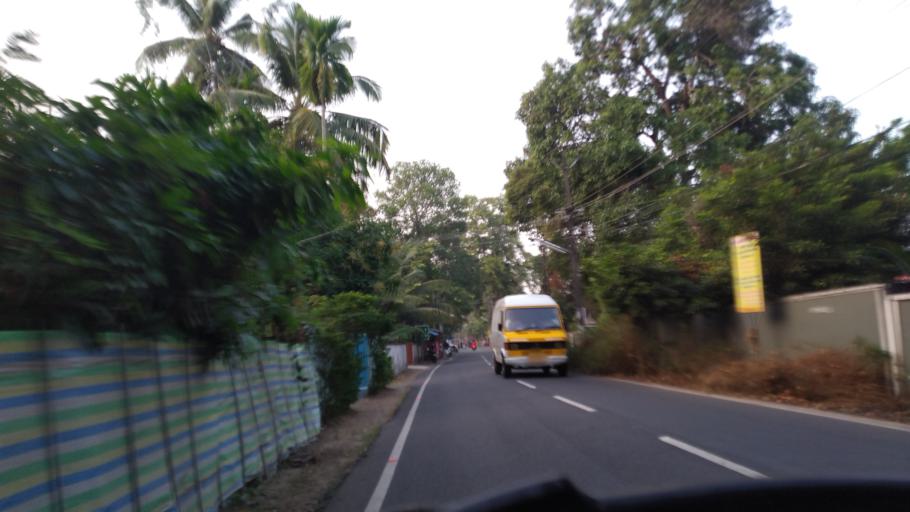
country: IN
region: Kerala
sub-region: Ernakulam
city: Elur
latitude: 10.1152
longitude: 76.2424
